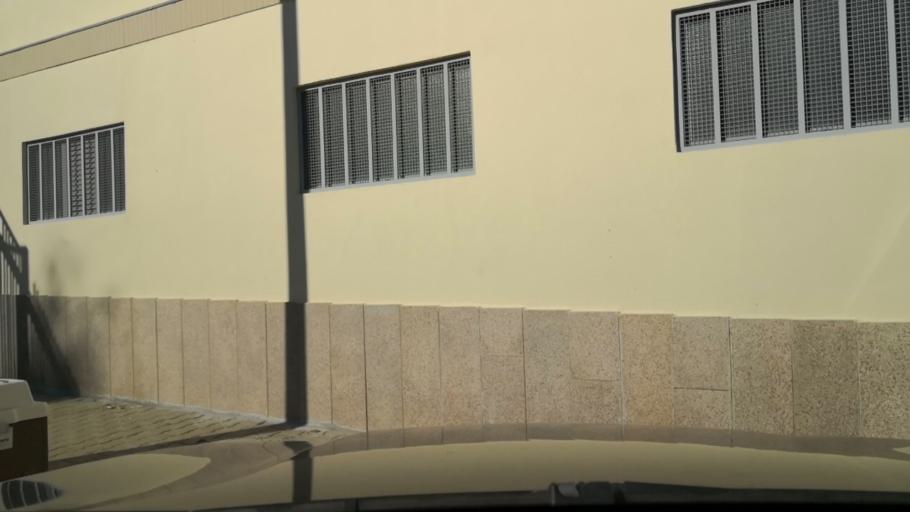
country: PT
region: Setubal
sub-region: Setubal
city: Setubal
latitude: 38.5239
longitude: -8.9086
